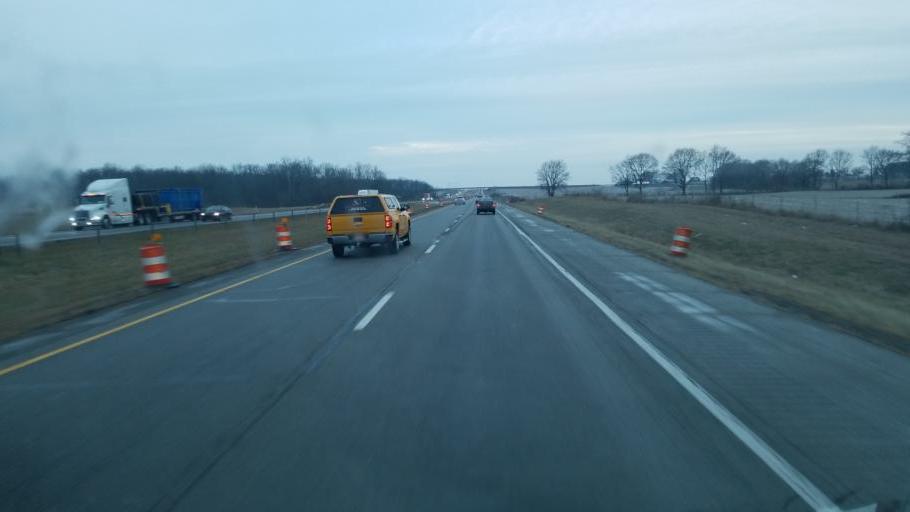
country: US
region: Indiana
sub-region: Henry County
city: Knightstown
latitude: 39.8294
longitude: -85.5930
